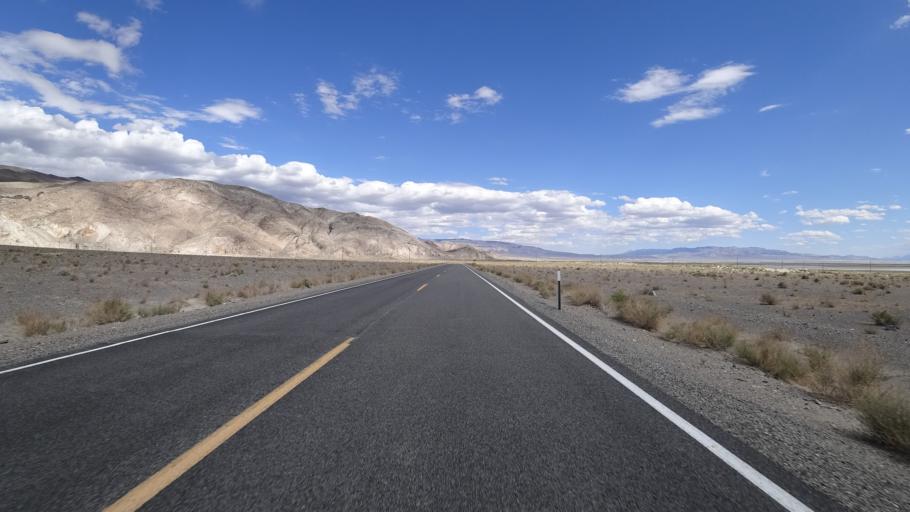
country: US
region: California
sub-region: Inyo County
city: Lone Pine
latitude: 36.5432
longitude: -117.9353
